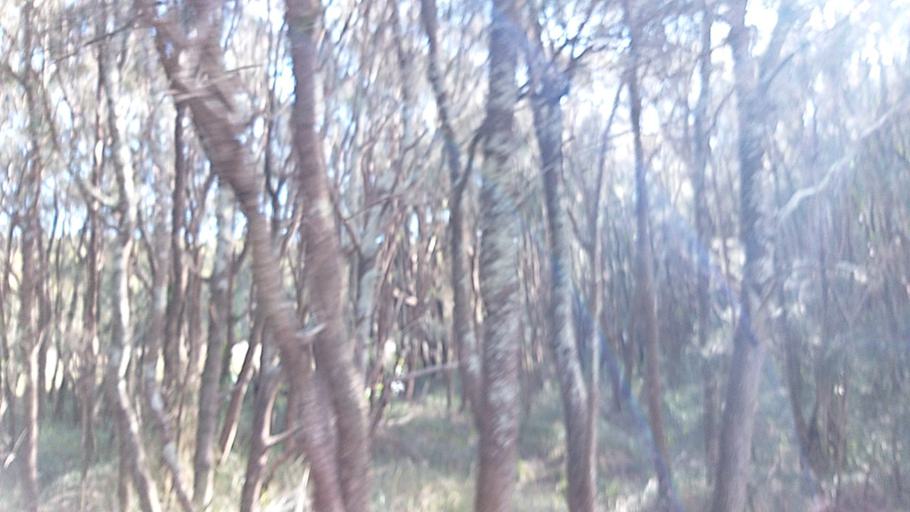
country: AU
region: New South Wales
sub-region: Wollongong
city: Fairy Meadow
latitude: -34.4026
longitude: 150.9021
